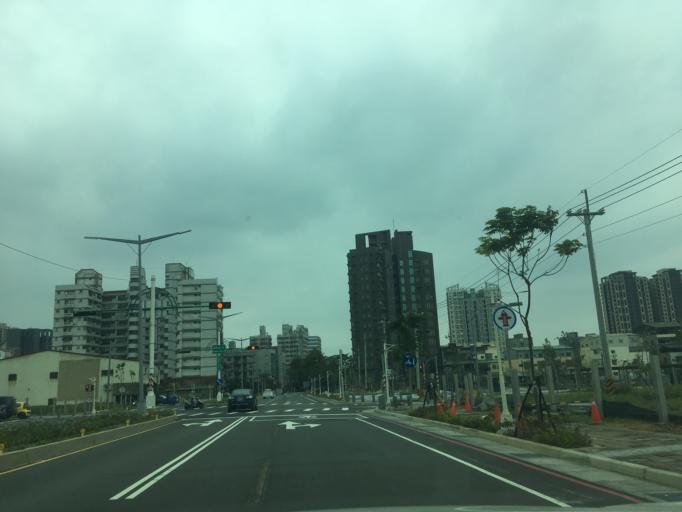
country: TW
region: Taiwan
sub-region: Taichung City
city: Taichung
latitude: 24.1791
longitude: 120.6768
